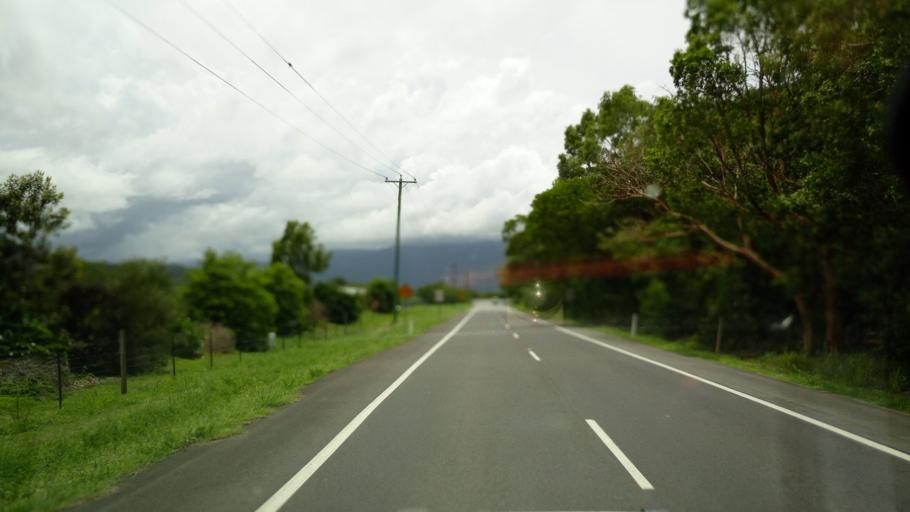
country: AU
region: Queensland
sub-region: Cairns
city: Redlynch
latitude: -16.8570
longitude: 145.7414
